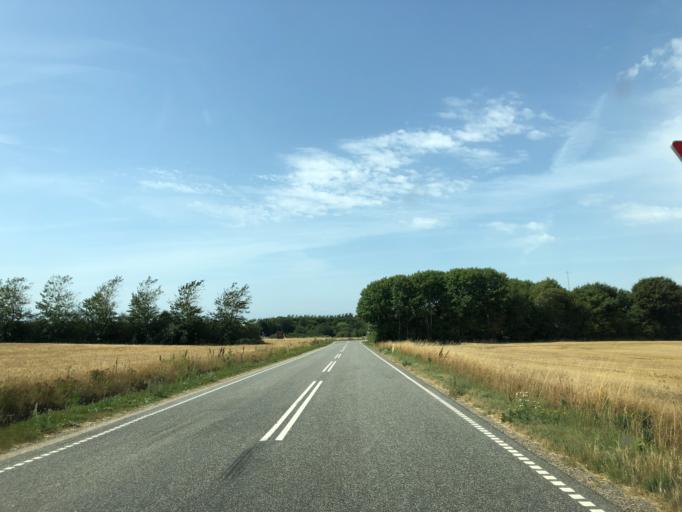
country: DK
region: Central Jutland
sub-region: Ringkobing-Skjern Kommune
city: Skjern
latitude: 56.0253
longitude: 8.4244
